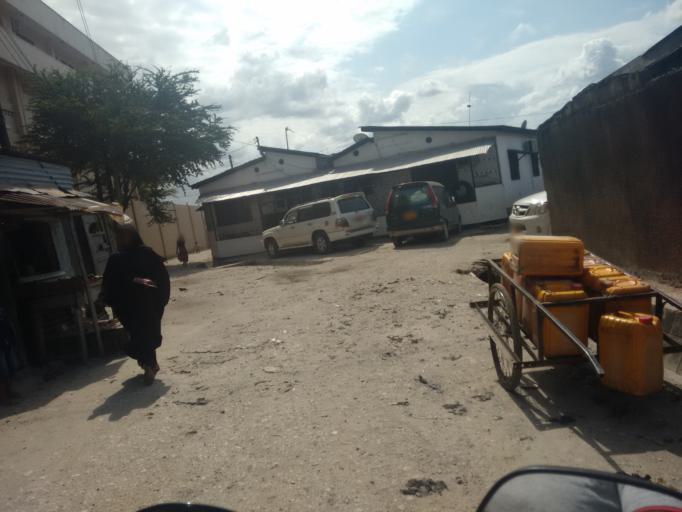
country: TZ
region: Dar es Salaam
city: Dar es Salaam
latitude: -6.8433
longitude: 39.2673
